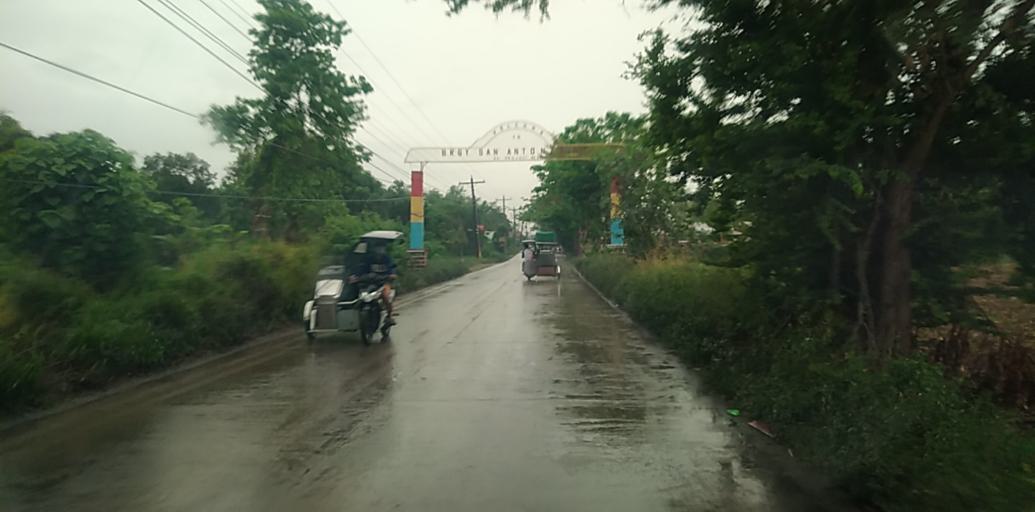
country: PH
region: Central Luzon
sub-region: Province of Pampanga
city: San Antonio
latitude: 15.1498
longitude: 120.6897
